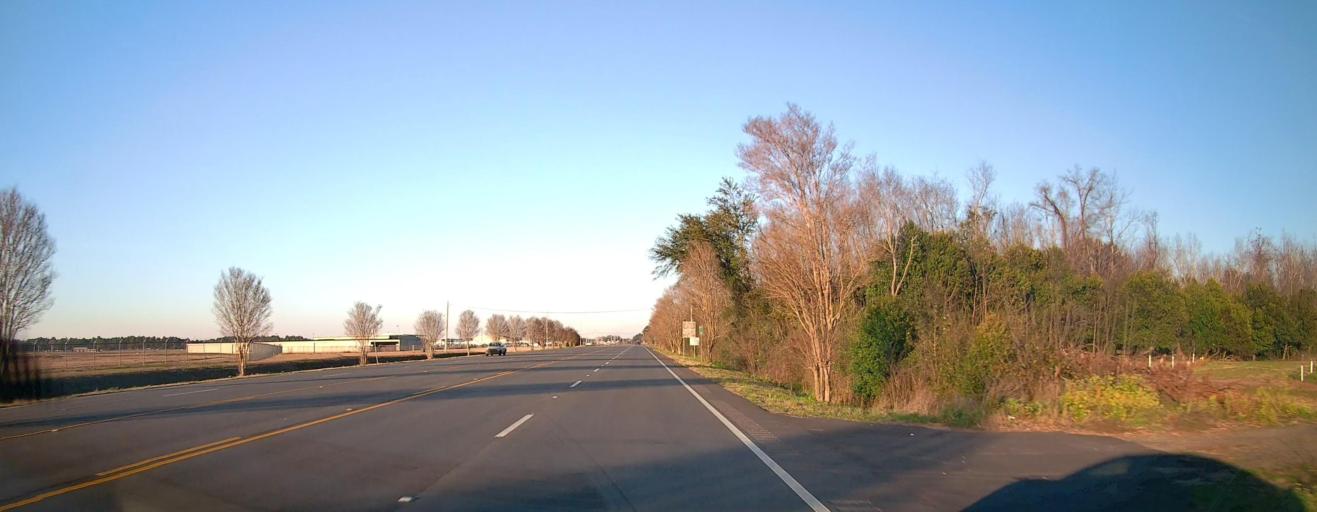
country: US
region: Georgia
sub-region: Dougherty County
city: Albany
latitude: 31.5274
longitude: -84.1907
